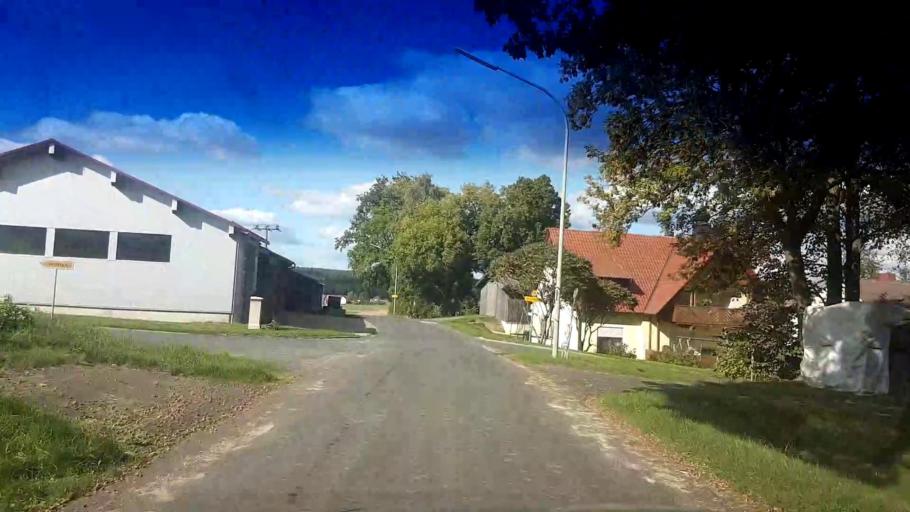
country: DE
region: Bavaria
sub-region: Upper Franconia
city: Schirnding
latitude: 50.0260
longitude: 12.2349
